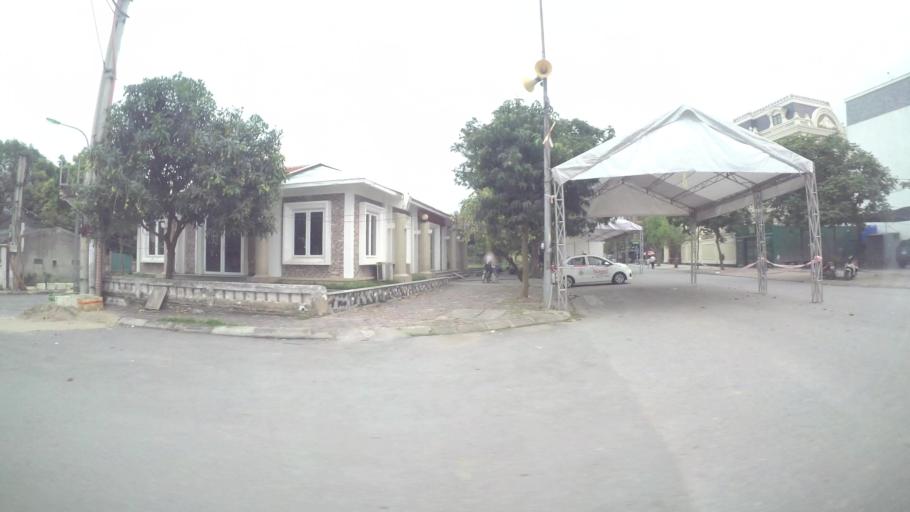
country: VN
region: Ha Noi
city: Trau Quy
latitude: 21.0536
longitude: 105.8989
